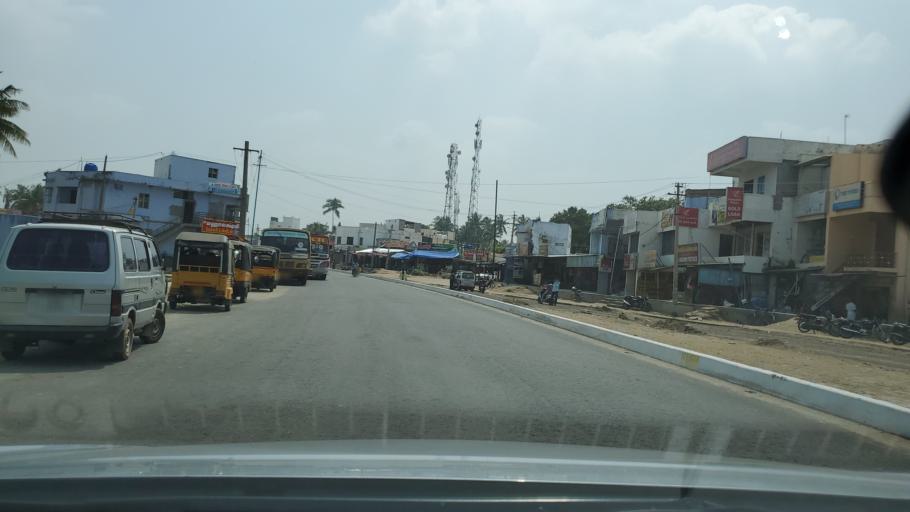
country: IN
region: Tamil Nadu
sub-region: Tiruppur
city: Kangayam
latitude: 10.9439
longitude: 77.4363
